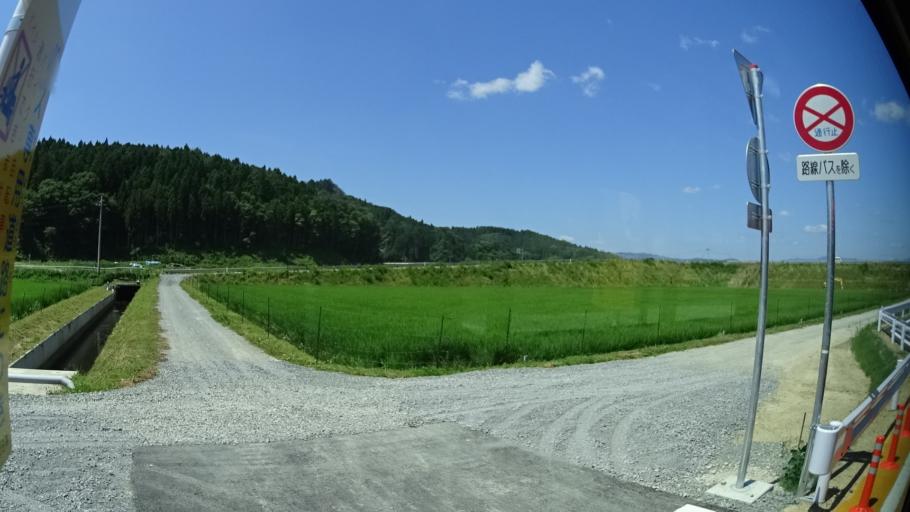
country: JP
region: Iwate
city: Ofunato
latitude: 38.9934
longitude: 141.6934
